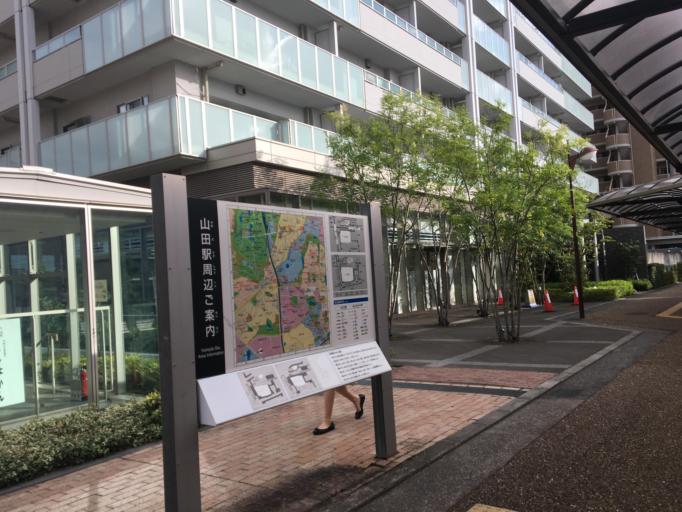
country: JP
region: Osaka
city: Suita
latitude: 34.8046
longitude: 135.5157
